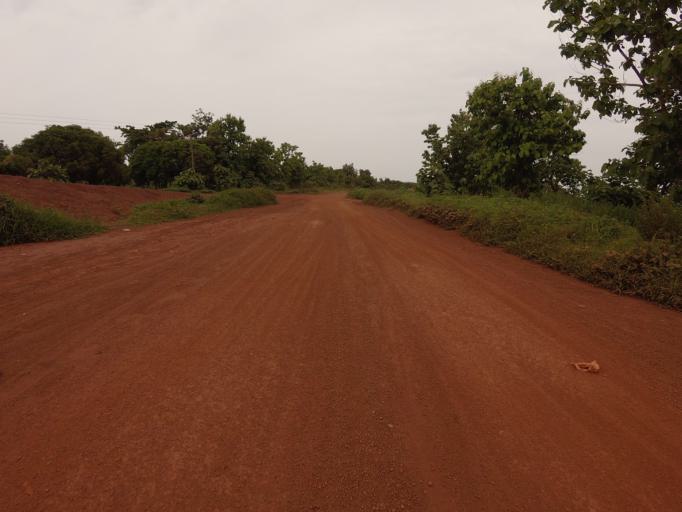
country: GH
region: Northern
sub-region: Yendi
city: Yendi
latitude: 9.0636
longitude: -0.0118
